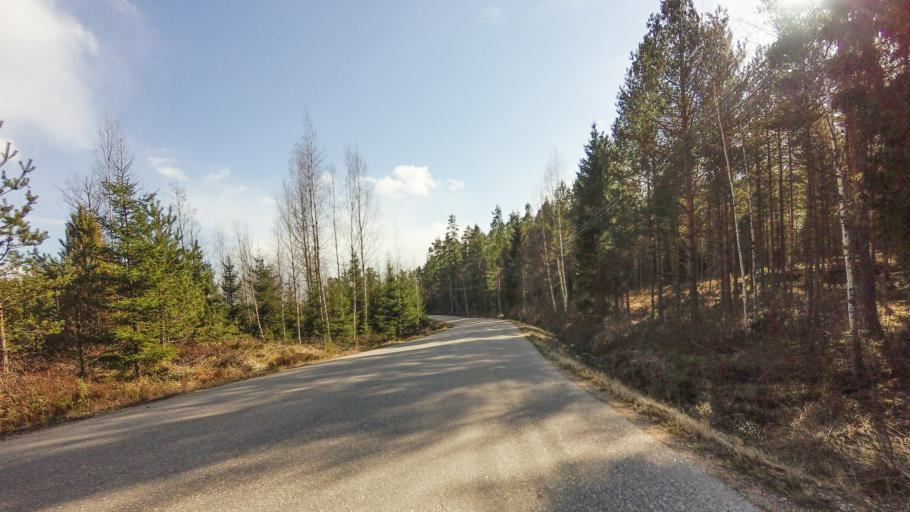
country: FI
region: Varsinais-Suomi
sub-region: Salo
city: Suomusjaervi
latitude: 60.3316
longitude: 23.6490
